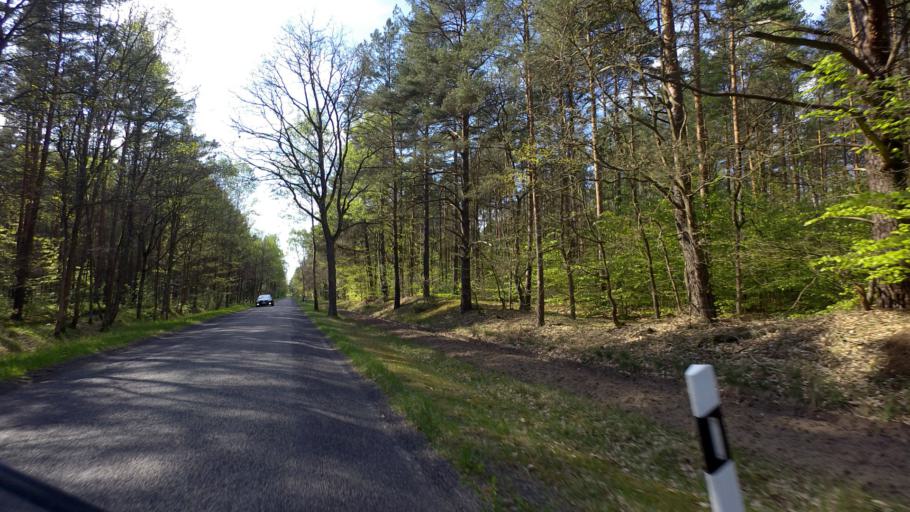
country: DE
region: Brandenburg
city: Zehdenick
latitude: 53.0145
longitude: 13.4208
